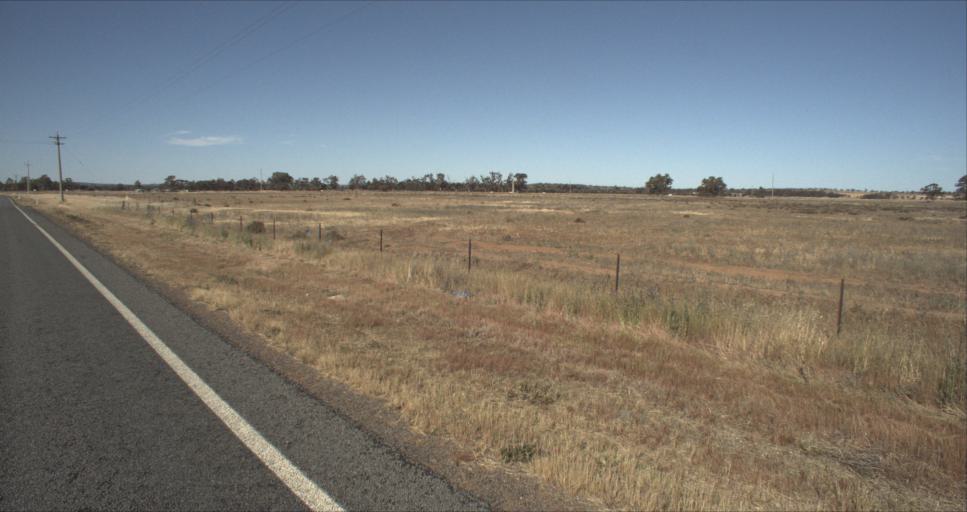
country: AU
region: New South Wales
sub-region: Leeton
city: Leeton
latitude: -34.6158
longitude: 146.4010
